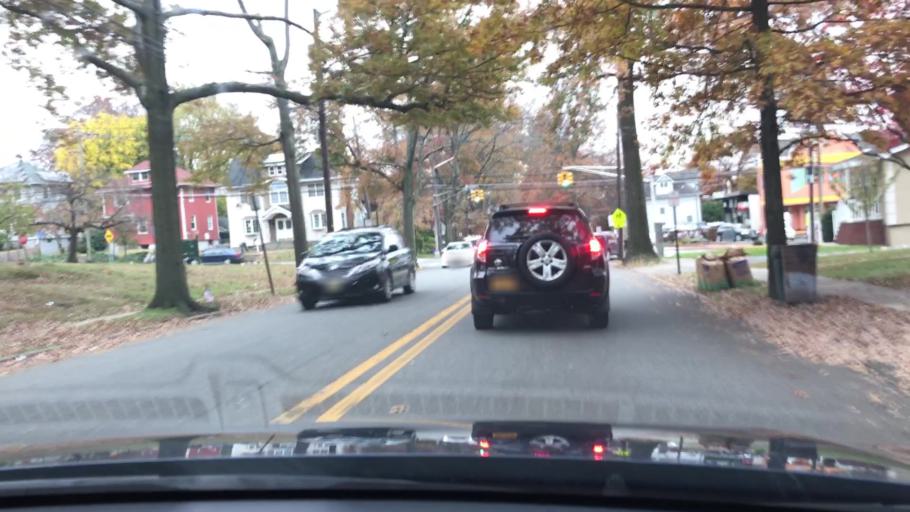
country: US
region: New Jersey
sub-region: Bergen County
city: Rutherford
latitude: 40.8383
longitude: -74.1160
